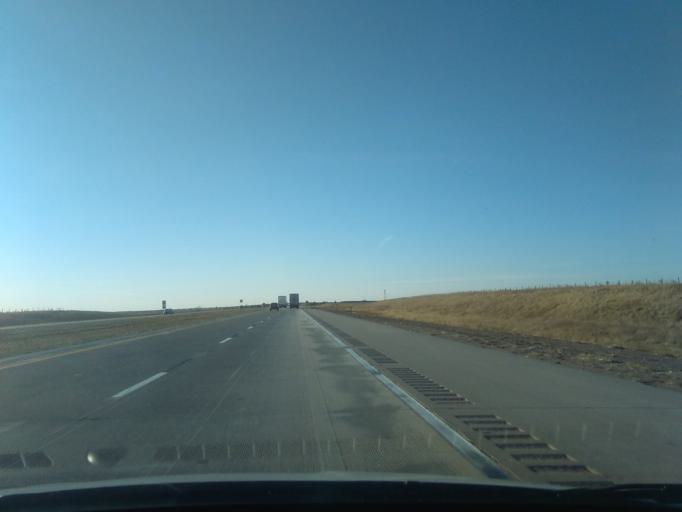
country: US
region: Nebraska
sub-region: Cheyenne County
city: Sidney
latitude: 41.1132
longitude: -102.7476
